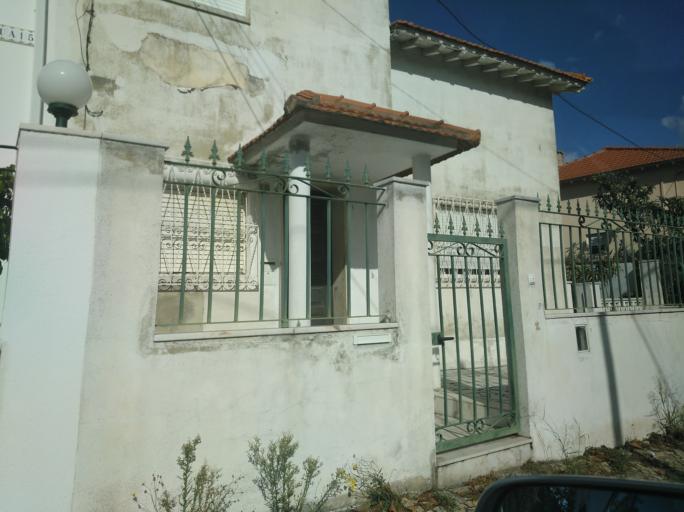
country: PT
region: Lisbon
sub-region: Loures
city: Moscavide
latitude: 38.7737
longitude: -9.1204
